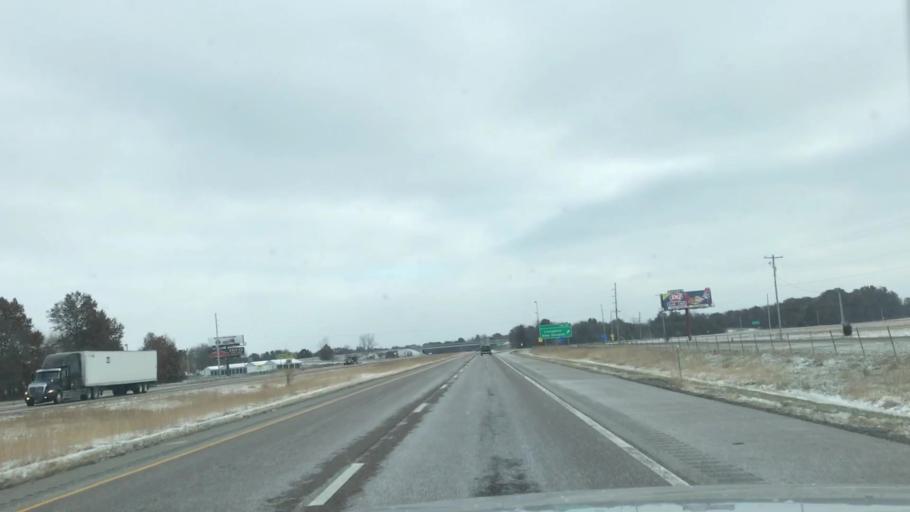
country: US
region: Illinois
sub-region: Macoupin County
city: Staunton
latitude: 38.9630
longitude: -89.7593
